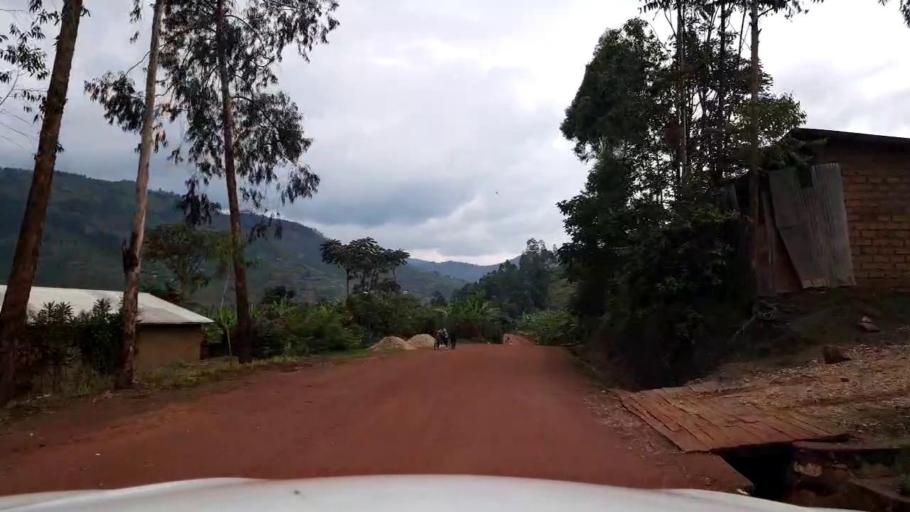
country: RW
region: Northern Province
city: Musanze
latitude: -1.6647
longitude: 29.8020
